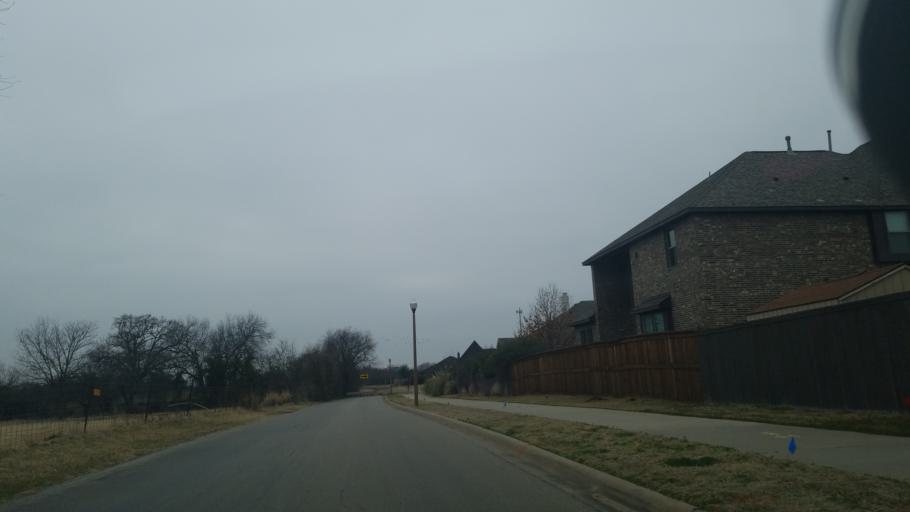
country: US
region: Texas
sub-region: Denton County
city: Denton
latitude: 33.1543
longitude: -97.1278
